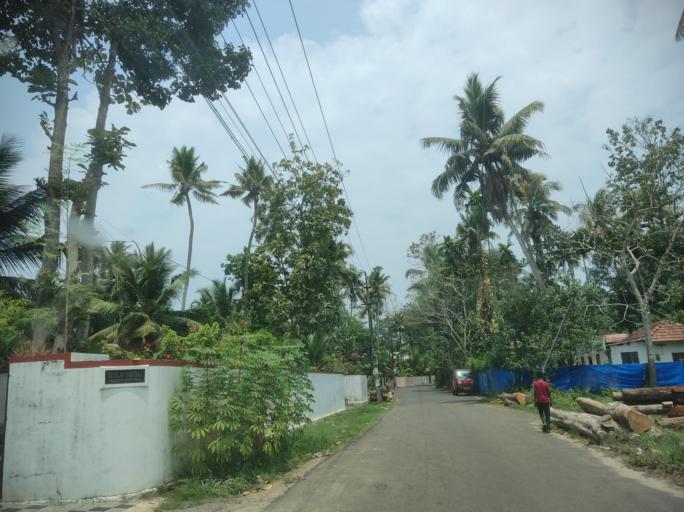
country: IN
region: Kerala
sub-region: Alappuzha
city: Vayalar
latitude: 9.7303
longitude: 76.3278
